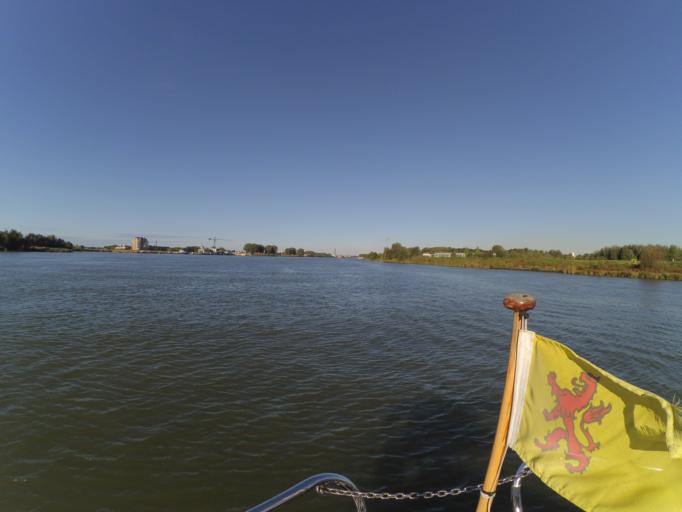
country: NL
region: South Holland
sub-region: Gemeente Zwijndrecht
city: Heerjansdam
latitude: 51.8078
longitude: 4.5870
